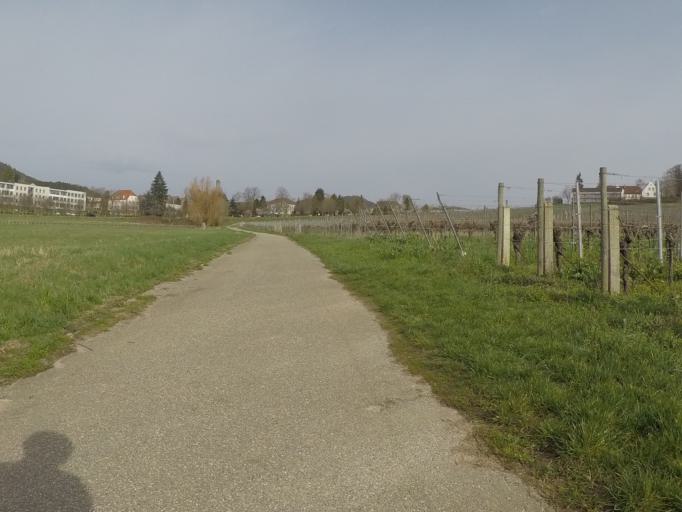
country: DE
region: Rheinland-Pfalz
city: Klingenmunster
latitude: 49.1473
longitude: 8.0188
